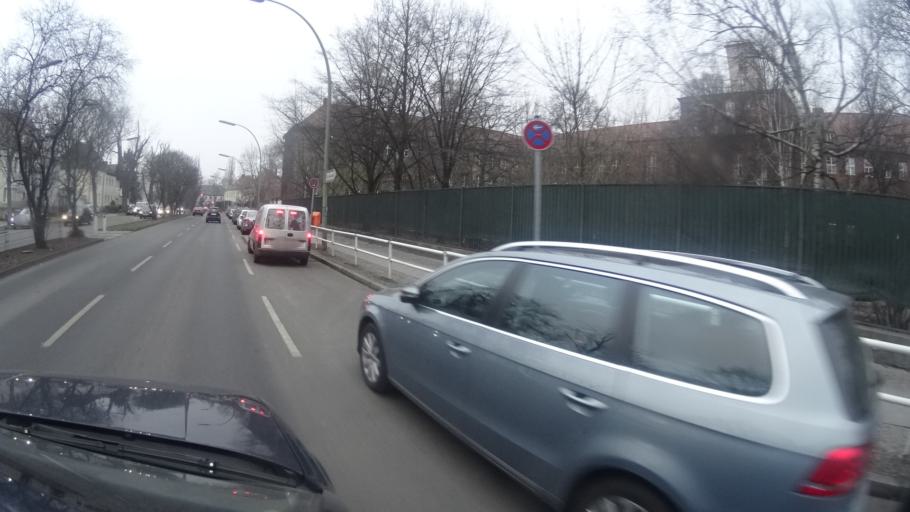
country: DE
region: Berlin
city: Tempelhof Bezirk
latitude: 52.4784
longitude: 13.3766
